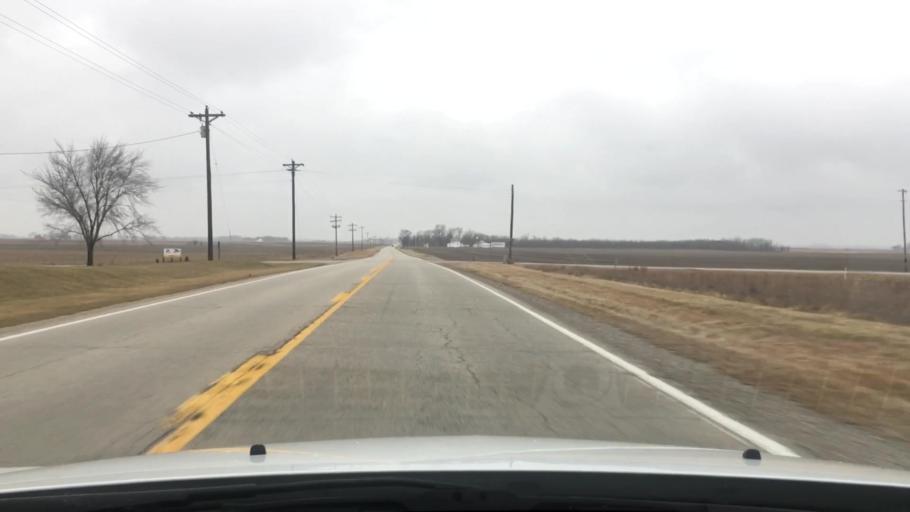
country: US
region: Illinois
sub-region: Iroquois County
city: Watseka
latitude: 40.8905
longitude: -87.7107
